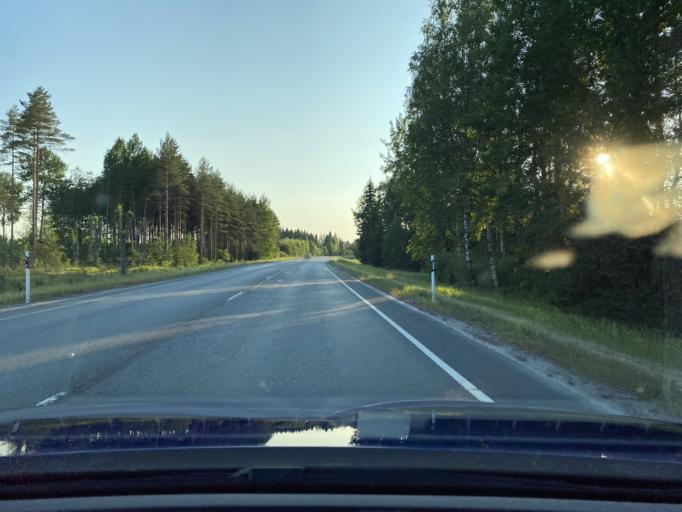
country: FI
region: Haeme
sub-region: Forssa
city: Tammela
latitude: 60.8261
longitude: 23.7520
